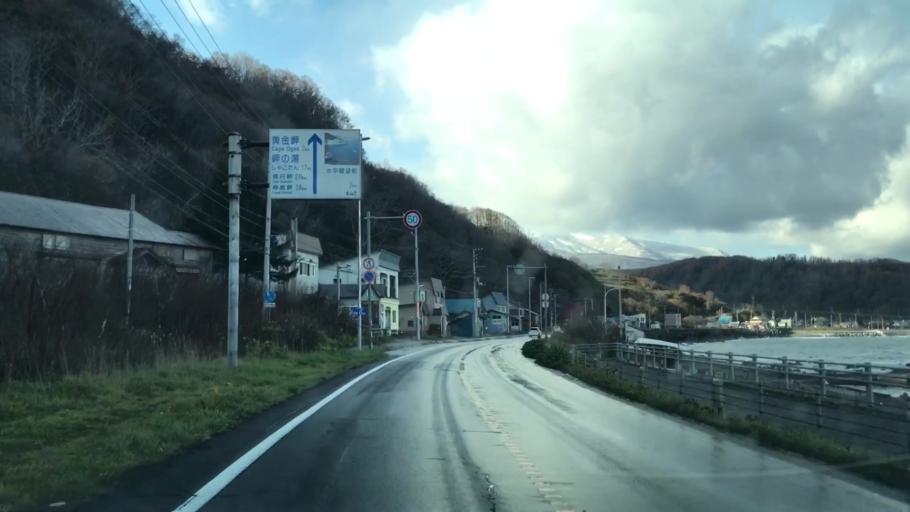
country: JP
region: Hokkaido
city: Yoichi
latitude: 43.2957
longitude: 140.6149
